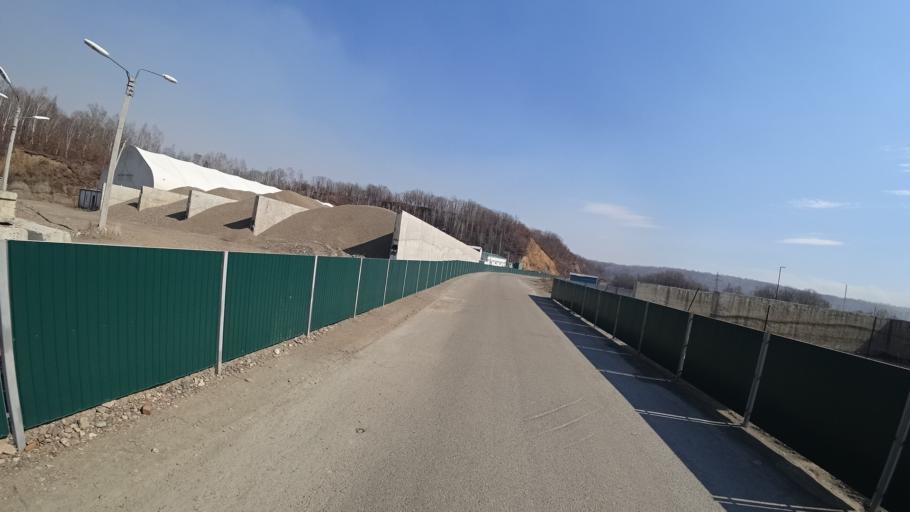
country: RU
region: Amur
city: Novobureyskiy
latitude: 49.7945
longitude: 129.9614
